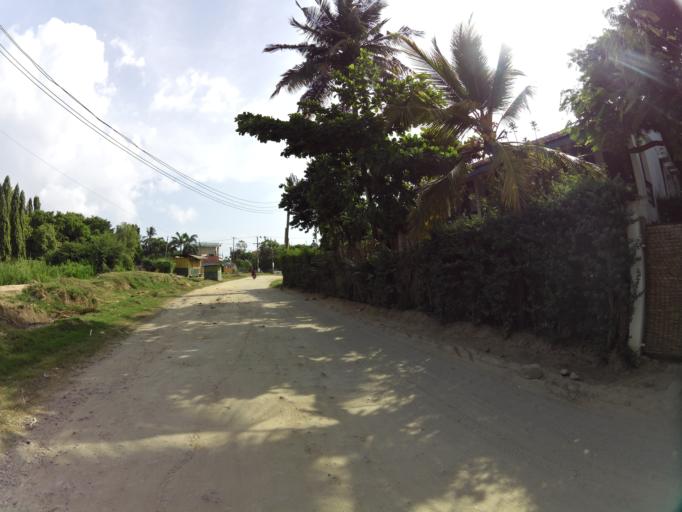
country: TZ
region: Dar es Salaam
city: Magomeni
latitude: -6.7687
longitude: 39.2497
